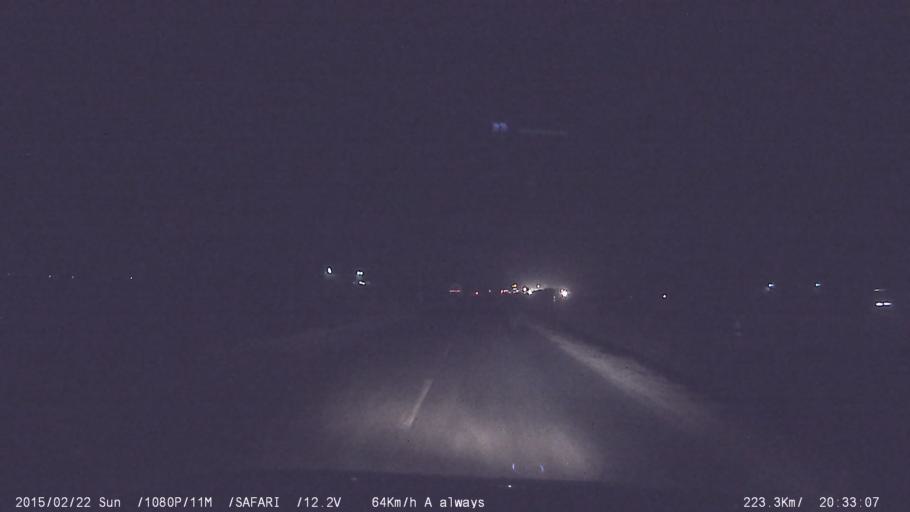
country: IN
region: Tamil Nadu
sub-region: Dindigul
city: Dindigul
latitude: 10.3542
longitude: 77.9493
